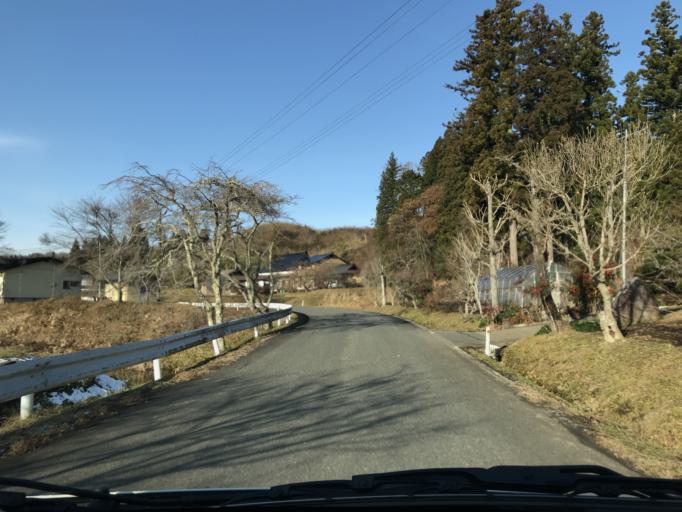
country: JP
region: Iwate
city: Ichinoseki
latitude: 38.9674
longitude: 141.0527
